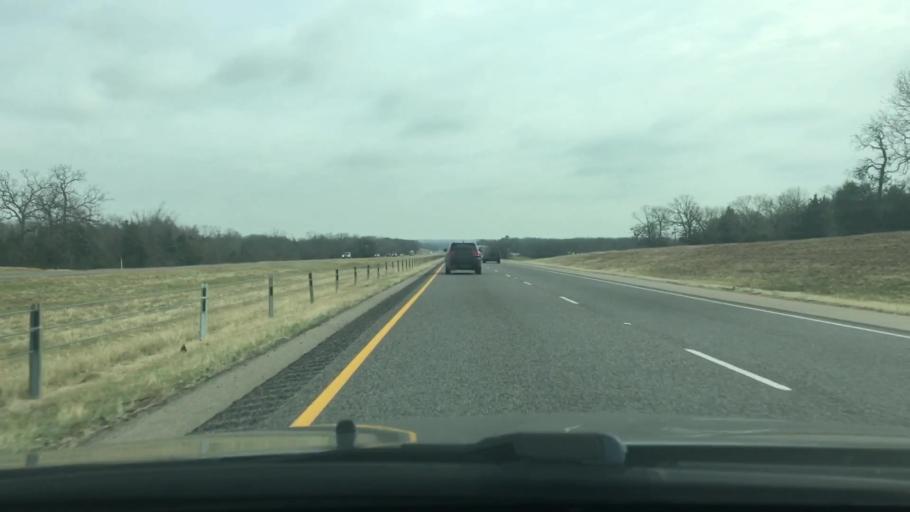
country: US
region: Texas
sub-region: Leon County
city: Buffalo
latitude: 31.5275
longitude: -96.1145
